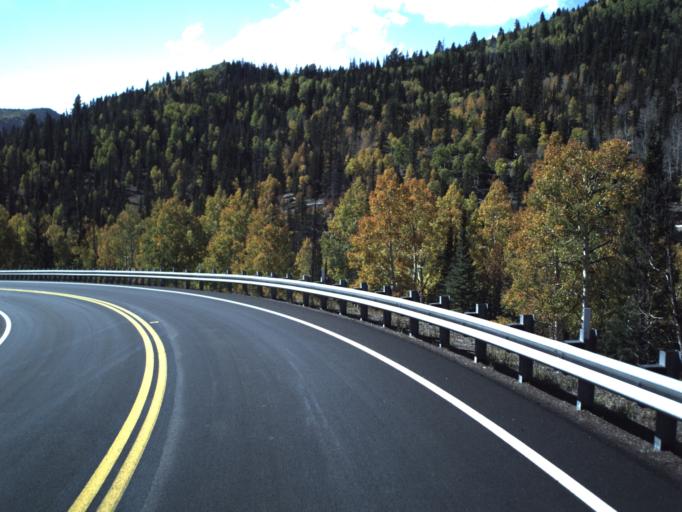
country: US
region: Utah
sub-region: Piute County
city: Junction
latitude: 38.3094
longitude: -112.4127
